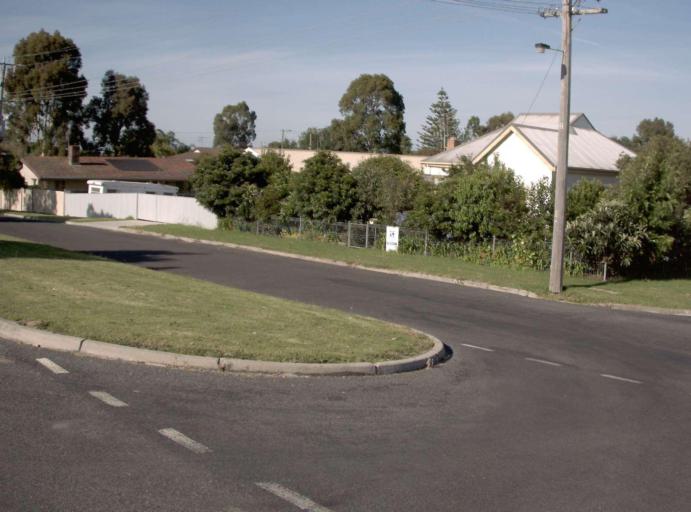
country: AU
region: Victoria
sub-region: East Gippsland
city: Lakes Entrance
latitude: -37.6948
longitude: 148.4579
